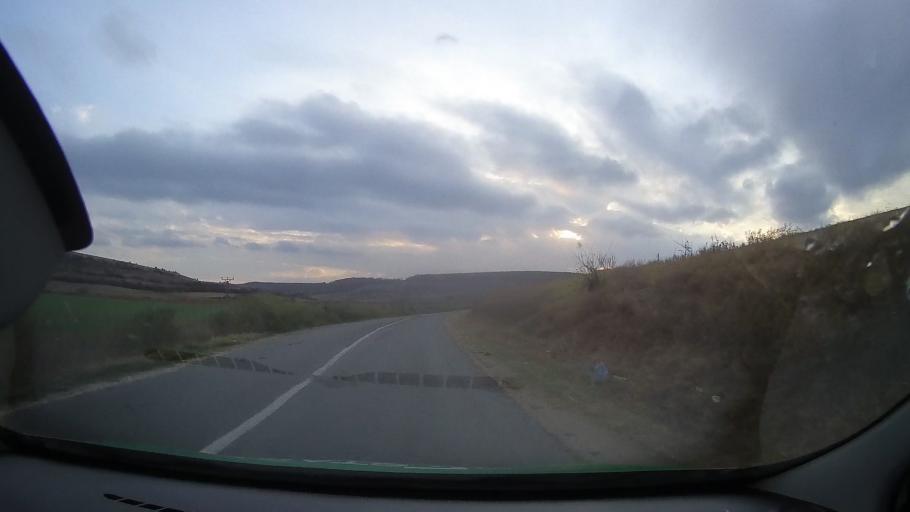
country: RO
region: Constanta
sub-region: Comuna Dobromir
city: Dobromir
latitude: 44.0221
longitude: 27.7903
